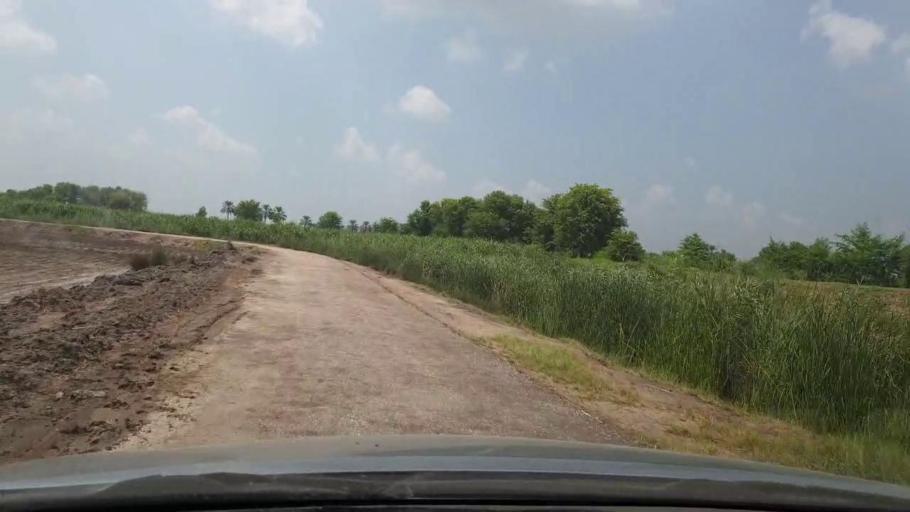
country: PK
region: Sindh
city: Kot Diji
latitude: 27.3952
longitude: 68.7252
